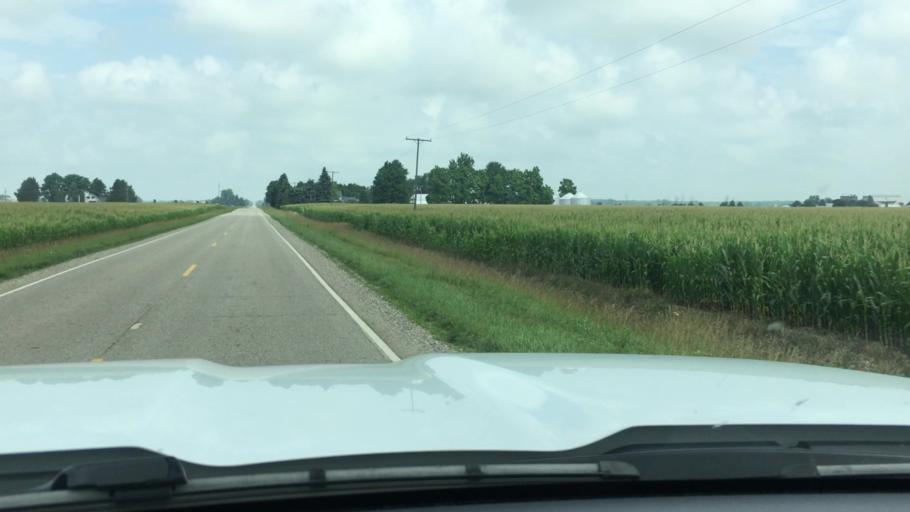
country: US
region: Michigan
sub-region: Sanilac County
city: Marlette
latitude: 43.3824
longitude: -83.0067
